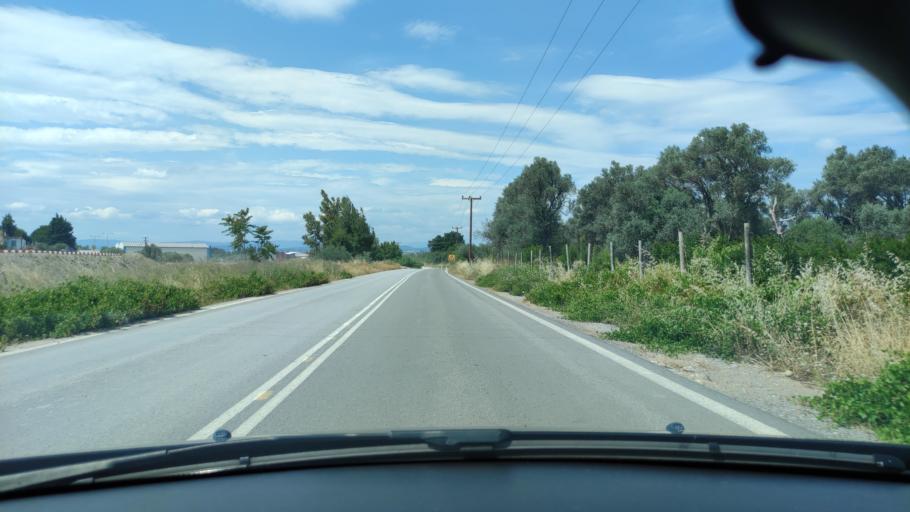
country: GR
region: Central Greece
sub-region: Nomos Evvoias
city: Filla
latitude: 38.4405
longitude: 23.6693
